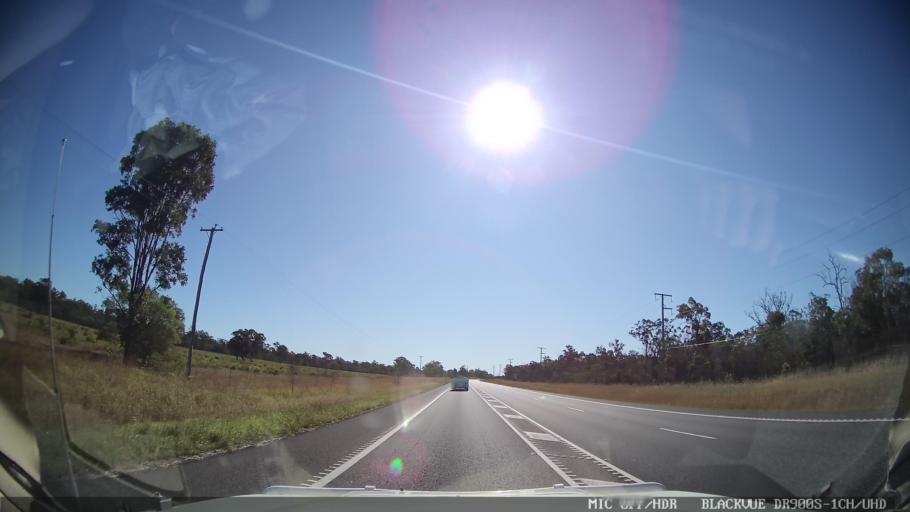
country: AU
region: Queensland
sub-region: Bundaberg
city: Childers
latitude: -25.2754
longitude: 152.3822
